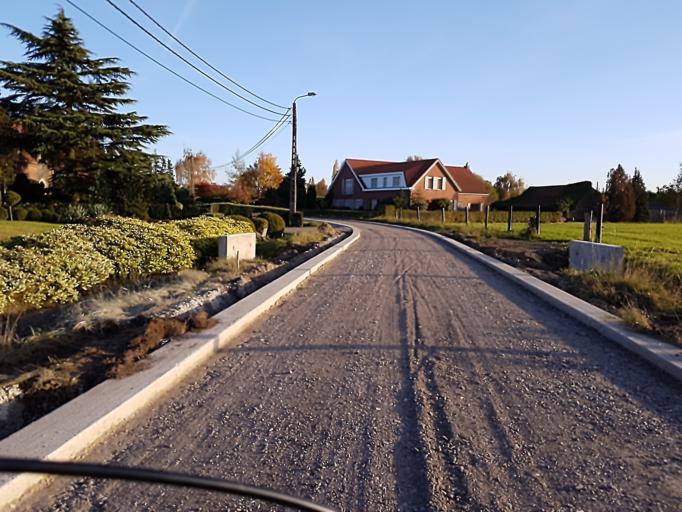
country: BE
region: Flanders
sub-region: Provincie Antwerpen
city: Bonheiden
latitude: 51.0523
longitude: 4.5822
